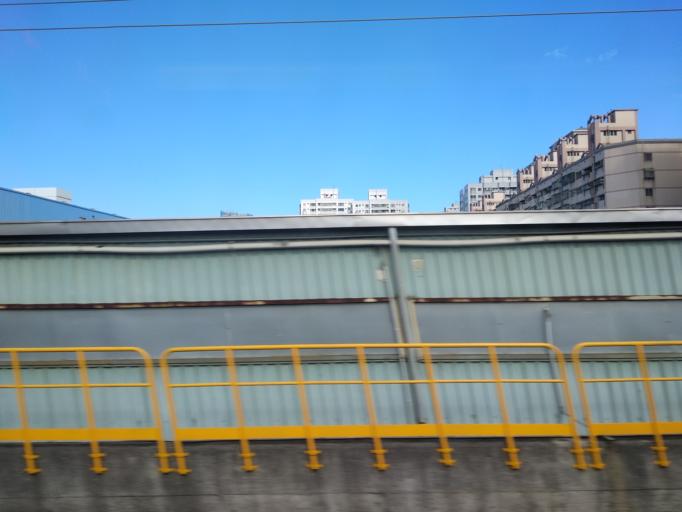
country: TW
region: Taiwan
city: Taoyuan City
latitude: 24.9837
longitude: 121.2873
